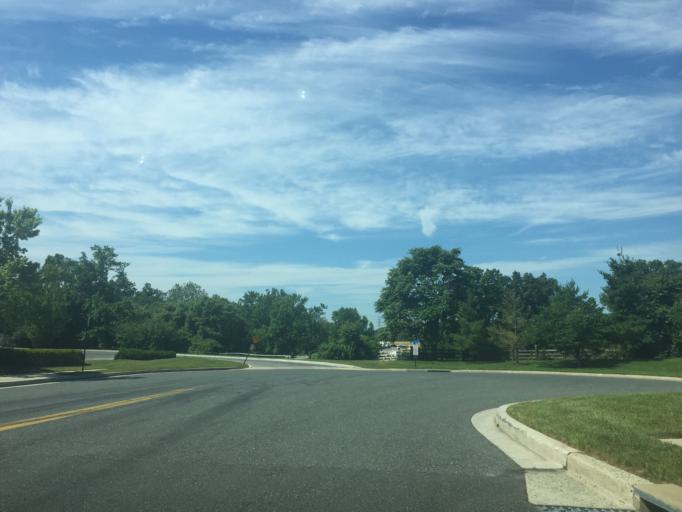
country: US
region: Maryland
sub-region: Baltimore County
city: Rossville
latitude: 39.3250
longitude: -76.4888
